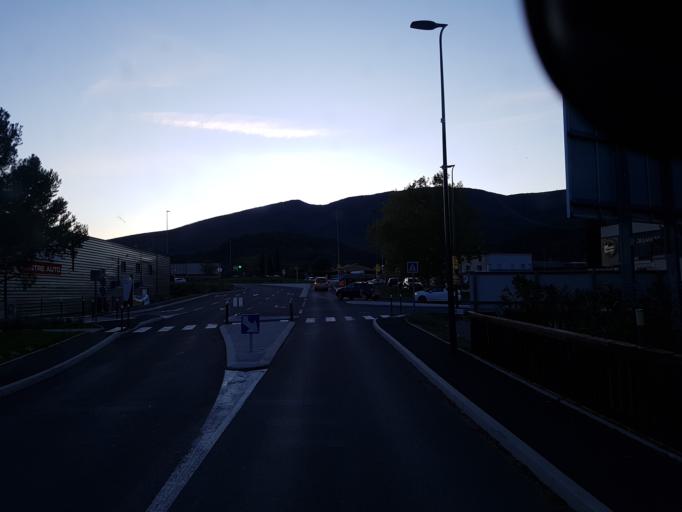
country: FR
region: Provence-Alpes-Cote d'Azur
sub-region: Departement des Alpes-de-Haute-Provence
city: Peipin
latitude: 44.1405
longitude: 5.9686
